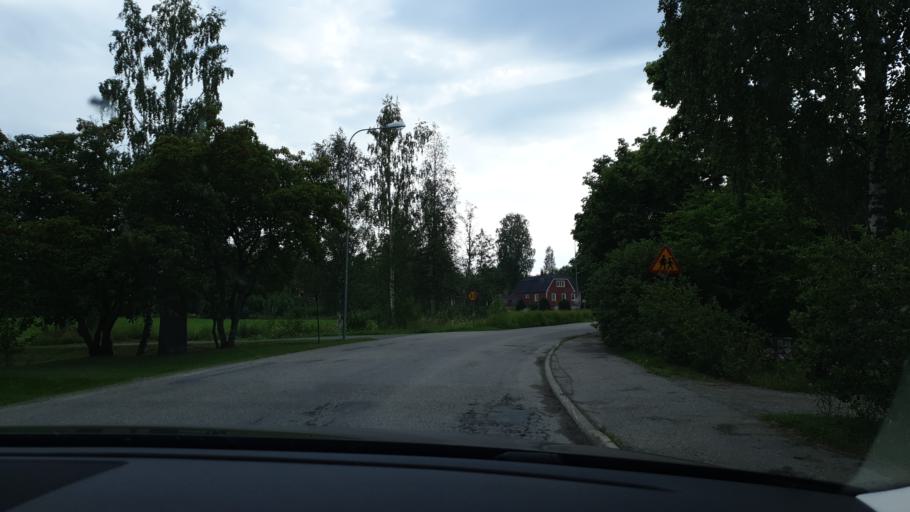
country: SE
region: Gaevleborg
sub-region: Hudiksvalls Kommun
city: Iggesund
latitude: 61.5449
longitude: 17.0050
